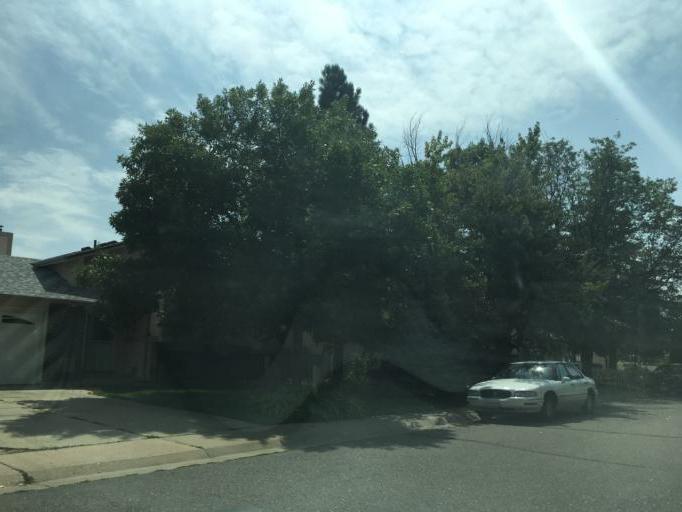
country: US
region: Colorado
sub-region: Adams County
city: Aurora
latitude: 39.7354
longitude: -104.7995
